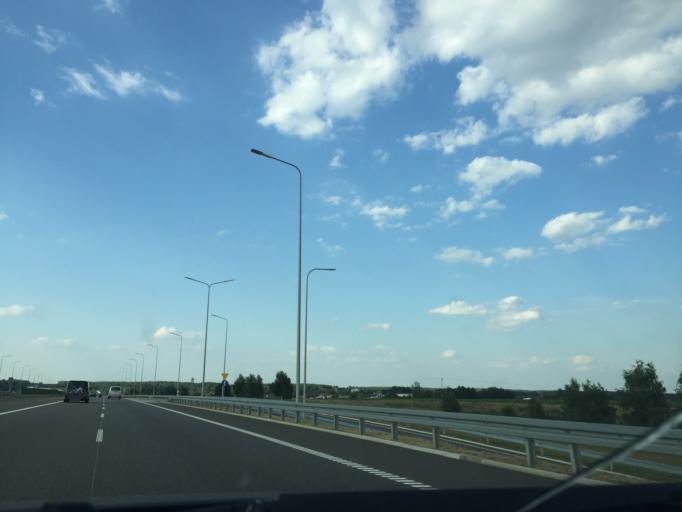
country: PL
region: Masovian Voivodeship
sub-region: Powiat radomski
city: Zakrzew
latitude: 51.4204
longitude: 21.0307
